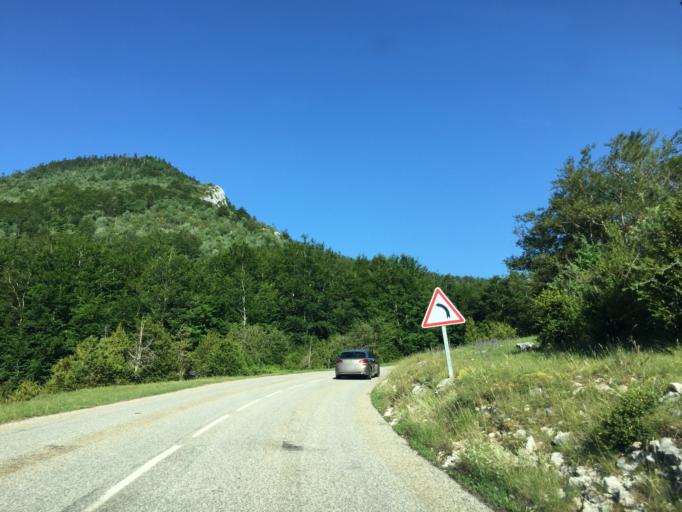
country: FR
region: Rhone-Alpes
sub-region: Departement de la Drome
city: Saint-Laurent-en-Royans
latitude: 44.9455
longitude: 5.3916
